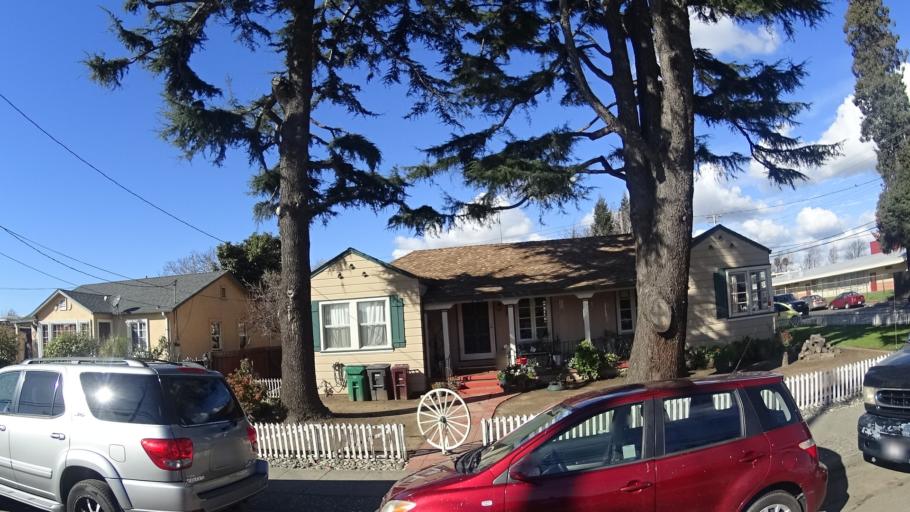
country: US
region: California
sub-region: Alameda County
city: San Lorenzo
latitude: 37.6683
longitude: -122.1149
